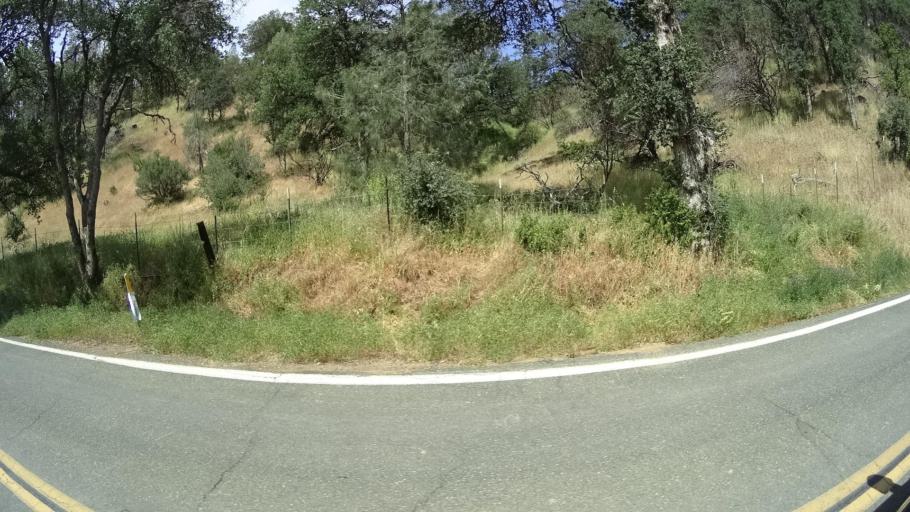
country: US
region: California
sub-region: Lake County
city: Lower Lake
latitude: 38.9058
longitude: -122.6390
